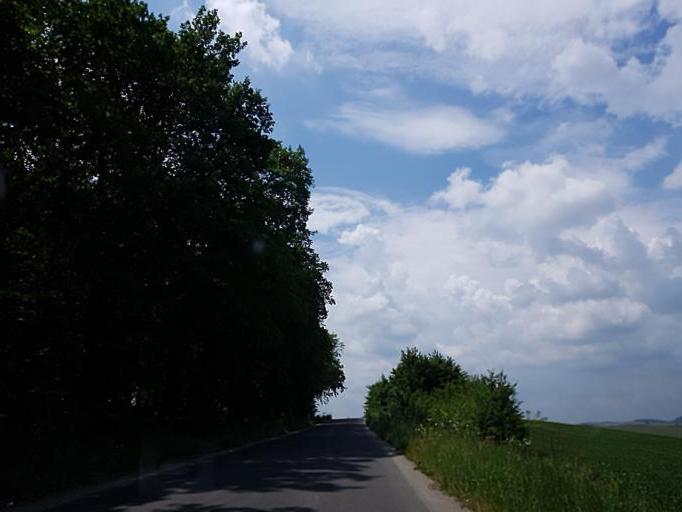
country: RO
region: Sibiu
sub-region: Comuna Seica Mica
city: Seica Mica
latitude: 46.0439
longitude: 24.1568
